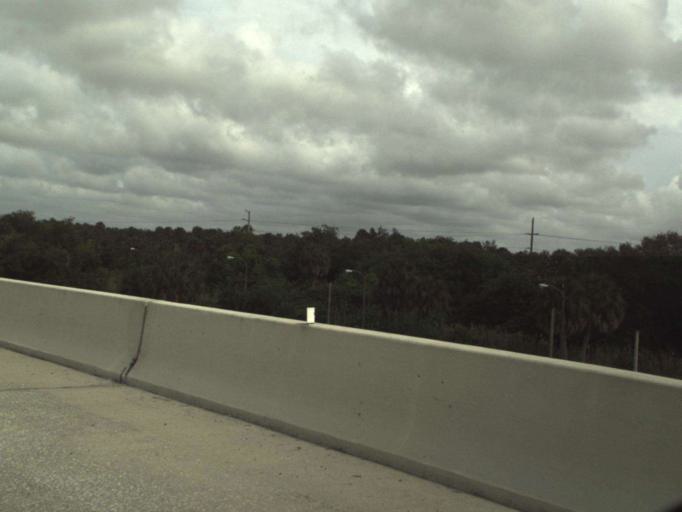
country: US
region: Florida
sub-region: Seminole County
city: Midway
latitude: 28.7857
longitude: -81.1804
